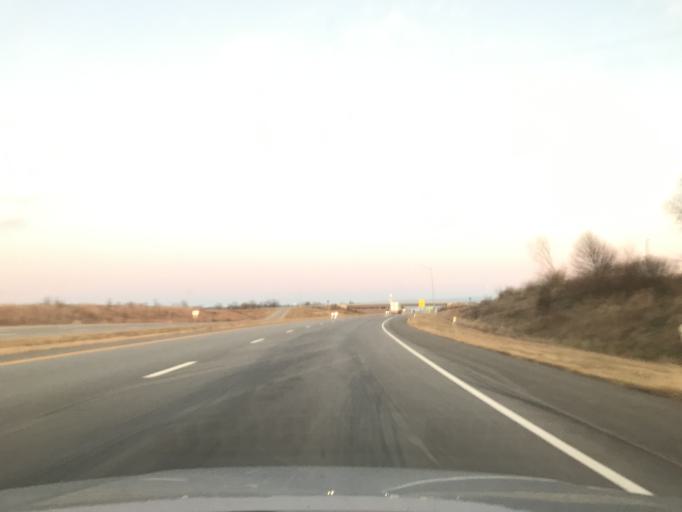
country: US
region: Missouri
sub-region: Marion County
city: Hannibal
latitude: 39.7132
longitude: -91.4517
